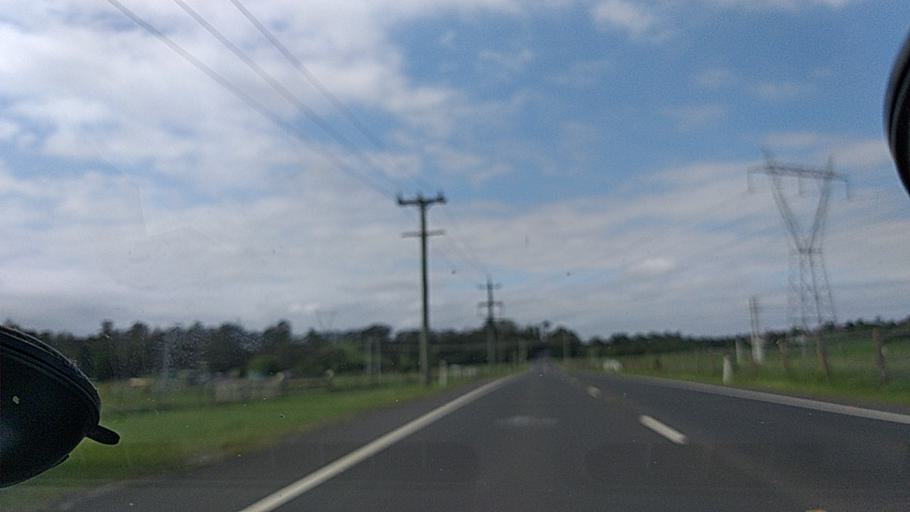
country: AU
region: New South Wales
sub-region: Campbelltown Municipality
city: Glen Alpine
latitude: -34.0962
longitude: 150.7684
